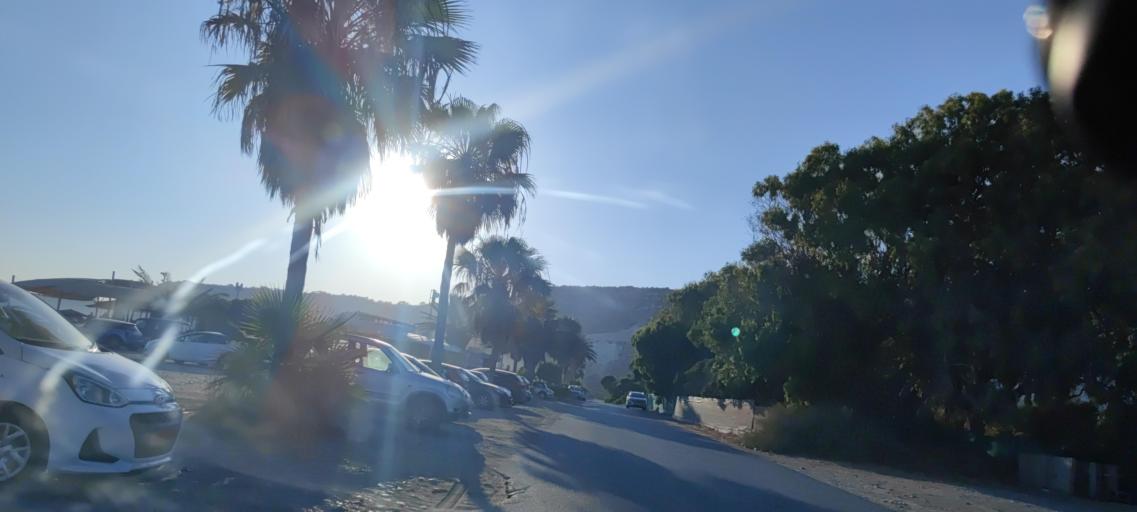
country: CY
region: Limassol
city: Erimi
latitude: 34.6645
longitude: 32.8802
